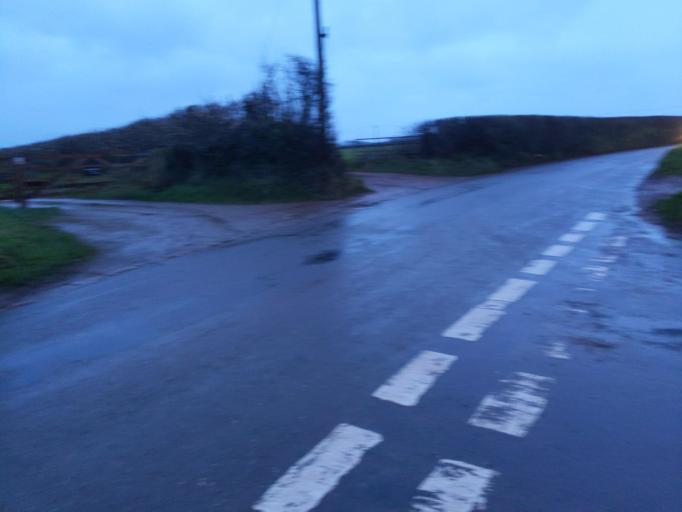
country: GB
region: England
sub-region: Devon
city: Yealmpton
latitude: 50.3338
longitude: -4.0137
